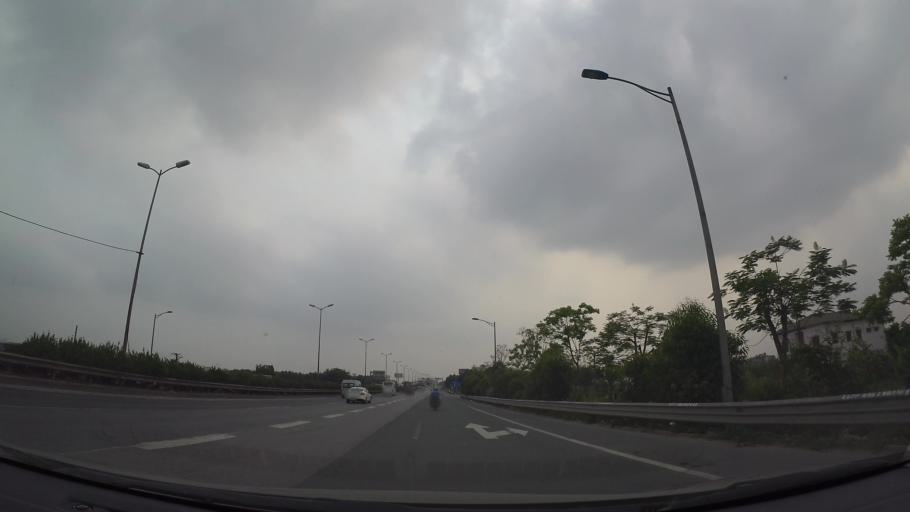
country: VN
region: Ha Noi
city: Trau Quy
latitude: 21.0082
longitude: 105.9145
